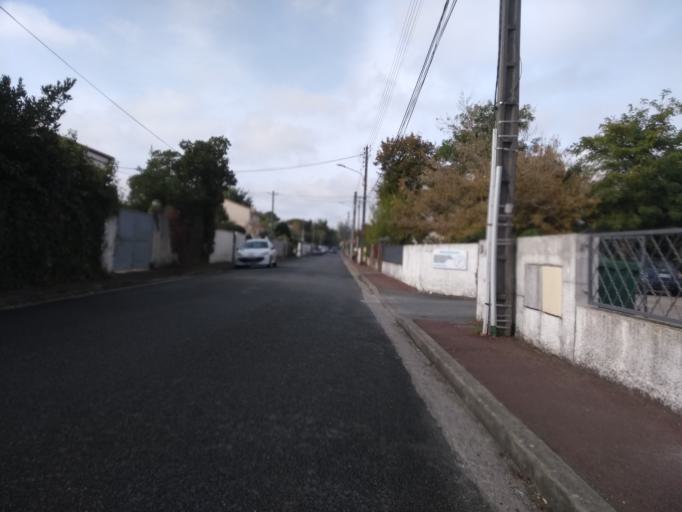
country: FR
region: Aquitaine
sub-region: Departement de la Gironde
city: Pessac
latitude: 44.8011
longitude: -0.6257
